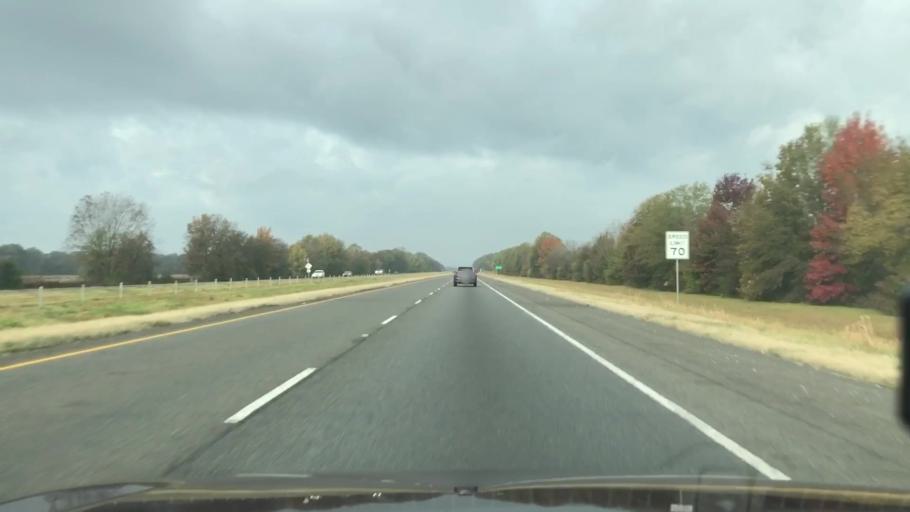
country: US
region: Louisiana
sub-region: Richland Parish
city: Delhi
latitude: 32.4334
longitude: -91.4314
